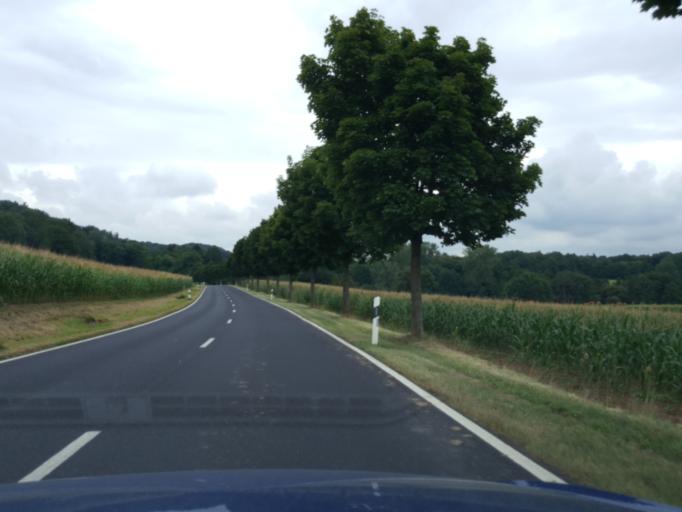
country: LU
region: Luxembourg
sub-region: Canton de Capellen
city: Kehlen
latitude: 49.6542
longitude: 6.0309
